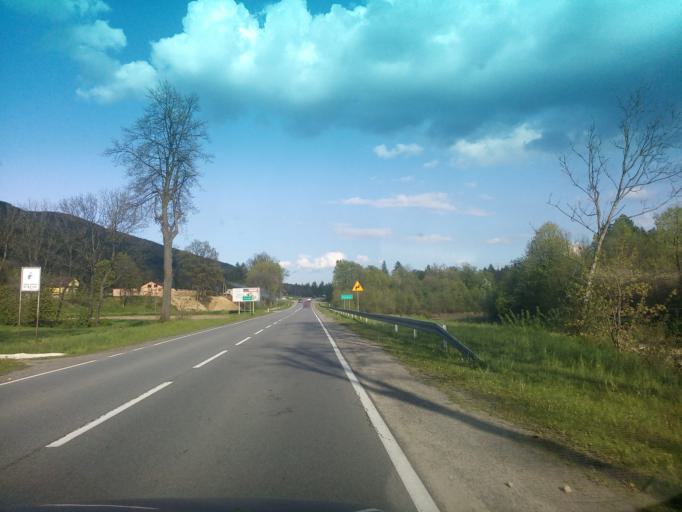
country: PL
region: Lesser Poland Voivodeship
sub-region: Powiat nowosadecki
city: Kamionka Wielka
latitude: 49.5387
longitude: 20.8065
